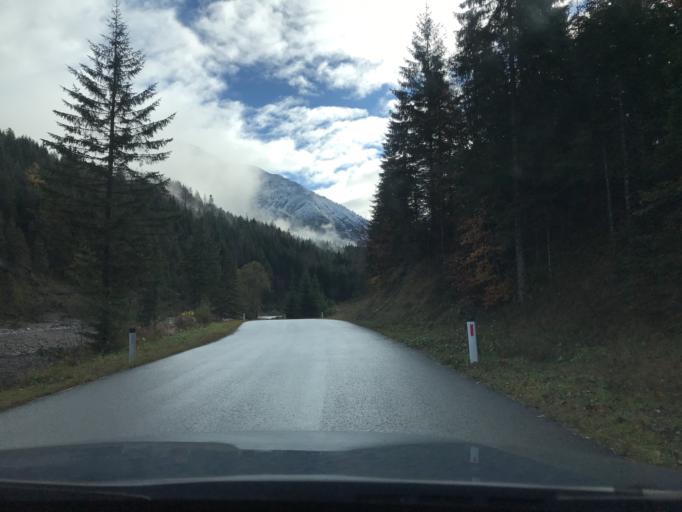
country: AT
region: Tyrol
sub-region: Politischer Bezirk Innsbruck Land
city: Gnadenwald
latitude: 47.4499
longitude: 11.5418
